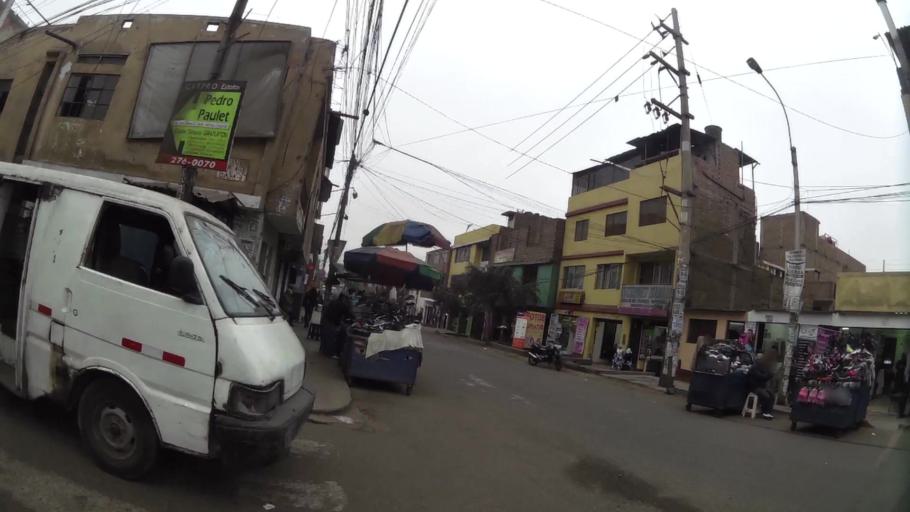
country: PE
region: Lima
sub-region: Lima
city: Surco
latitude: -12.1514
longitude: -76.9716
